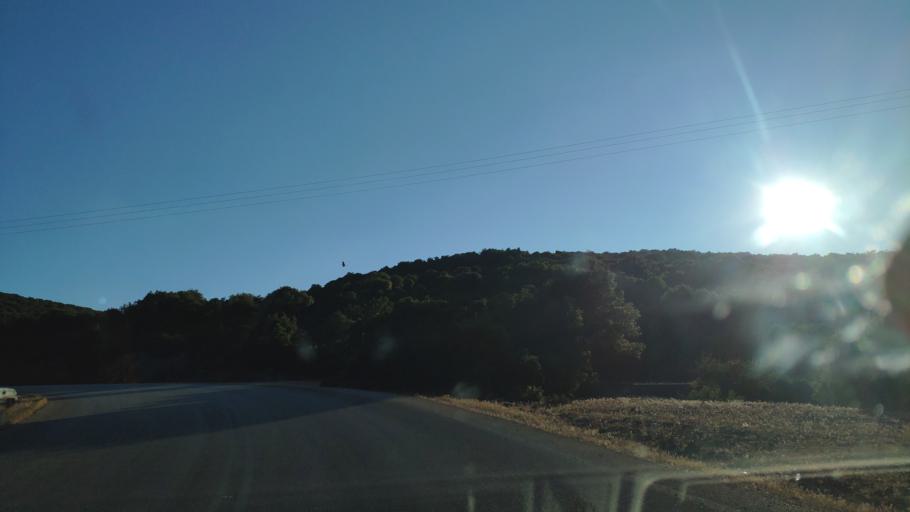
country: GR
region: West Greece
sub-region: Nomos Aitolias kai Akarnanias
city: Astakos
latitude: 38.6107
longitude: 21.1340
